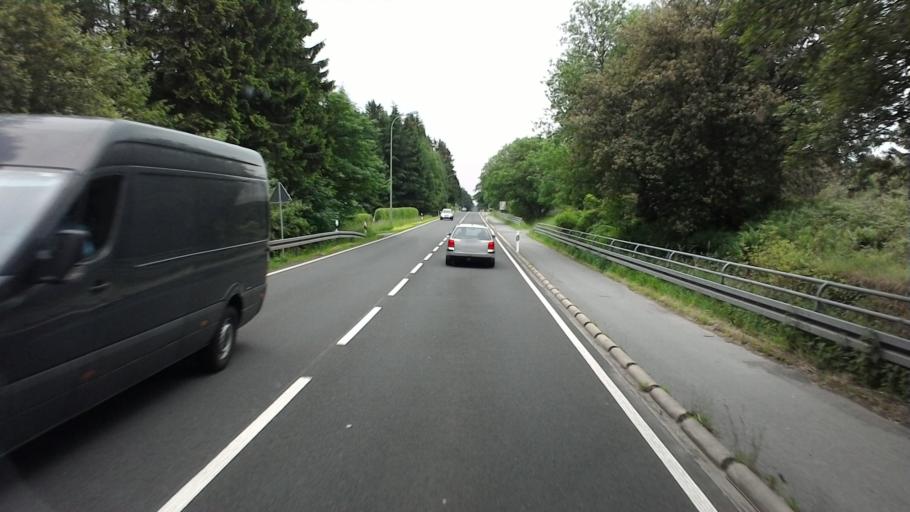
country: DE
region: North Rhine-Westphalia
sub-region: Regierungsbezirk Koln
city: Monschau
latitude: 50.6024
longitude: 6.2477
